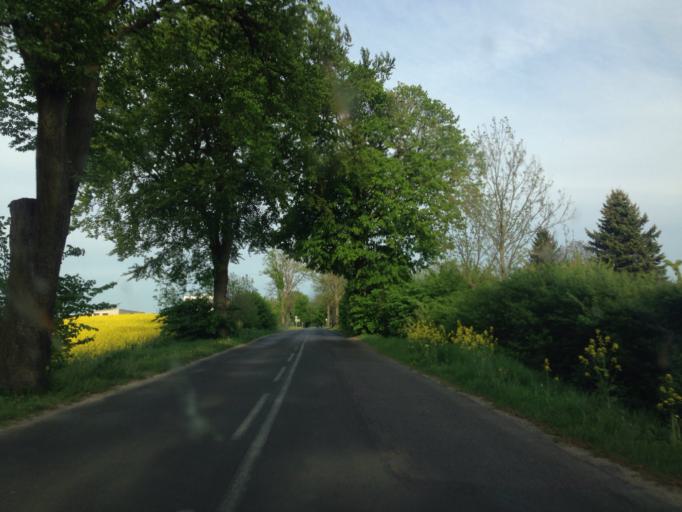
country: PL
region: Kujawsko-Pomorskie
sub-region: Powiat wabrzeski
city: Wabrzezno
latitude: 53.2809
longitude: 18.9208
